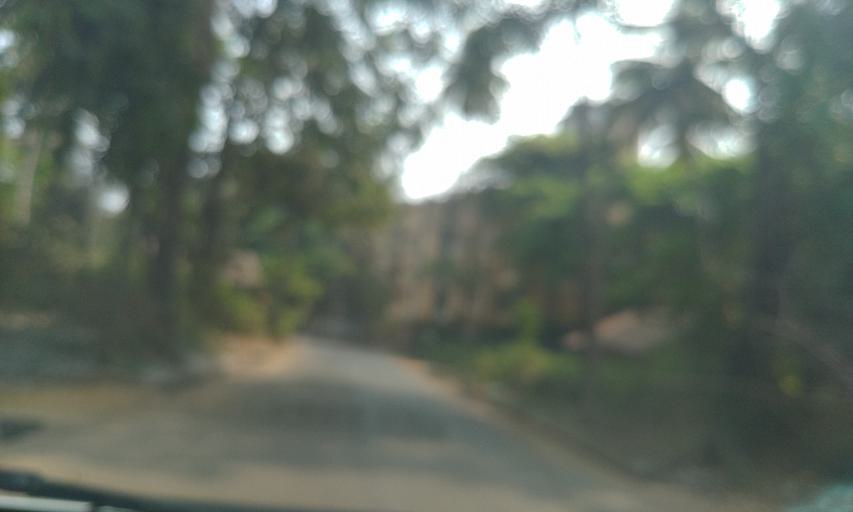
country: IN
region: Goa
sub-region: North Goa
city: Taleigao
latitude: 15.4681
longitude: 73.8219
